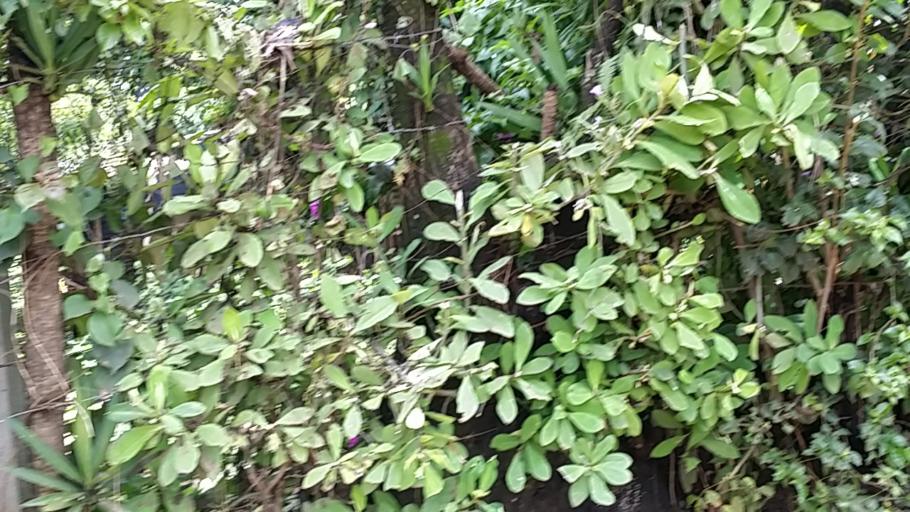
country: GT
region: Santa Rosa
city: Pueblo Nuevo Vinas
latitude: 14.3312
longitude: -90.5150
